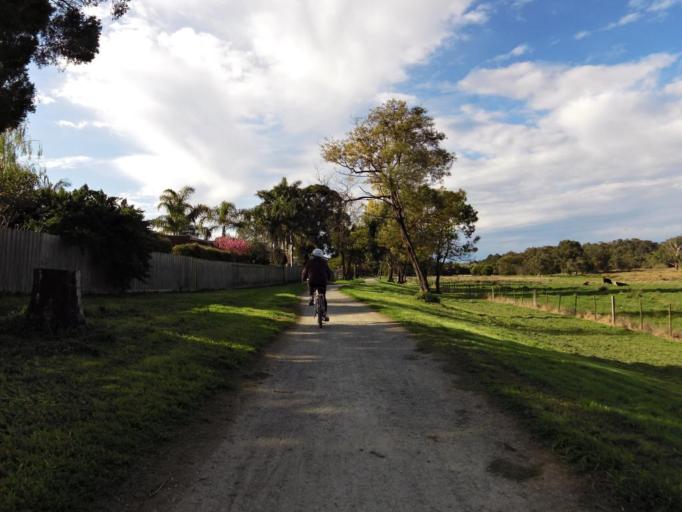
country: AU
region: Victoria
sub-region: Whitehorse
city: Vermont South
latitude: -37.8675
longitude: 145.1890
